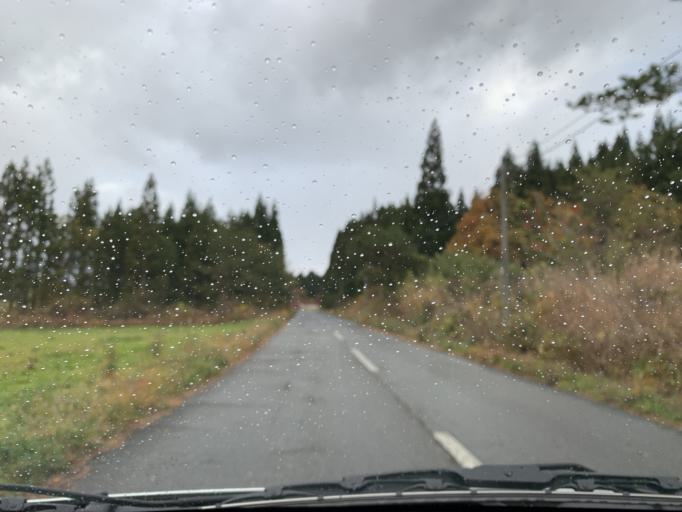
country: JP
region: Iwate
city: Mizusawa
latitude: 39.0897
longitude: 141.0001
